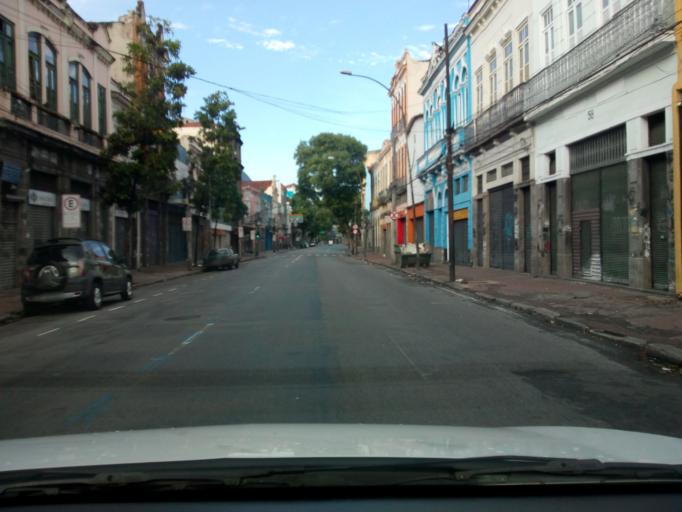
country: BR
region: Rio de Janeiro
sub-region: Rio De Janeiro
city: Rio de Janeiro
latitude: -22.9097
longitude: -43.1908
